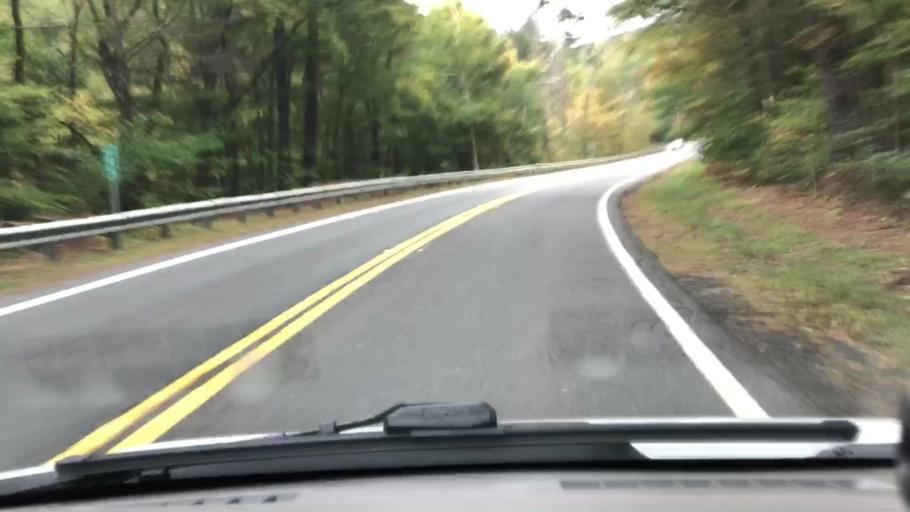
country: US
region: Massachusetts
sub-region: Hampshire County
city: Chesterfield
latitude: 42.3385
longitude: -72.8855
